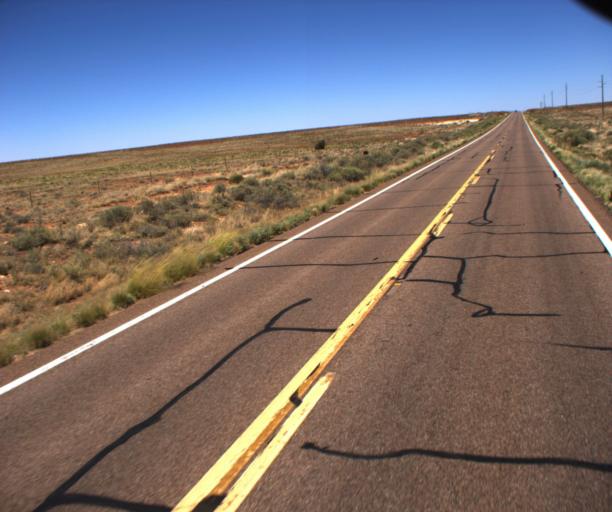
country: US
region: Arizona
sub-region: Coconino County
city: LeChee
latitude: 34.9094
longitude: -110.8385
